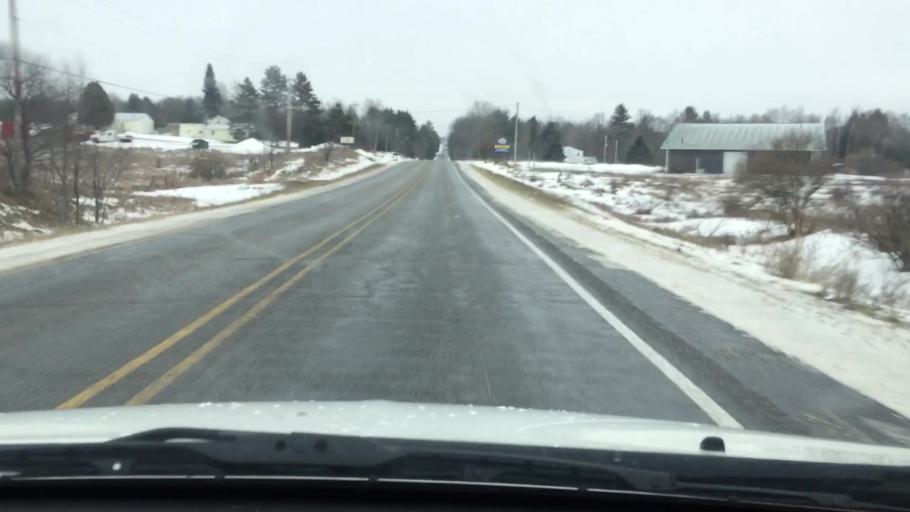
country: US
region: Michigan
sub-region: Wexford County
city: Cadillac
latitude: 44.0625
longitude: -85.4440
